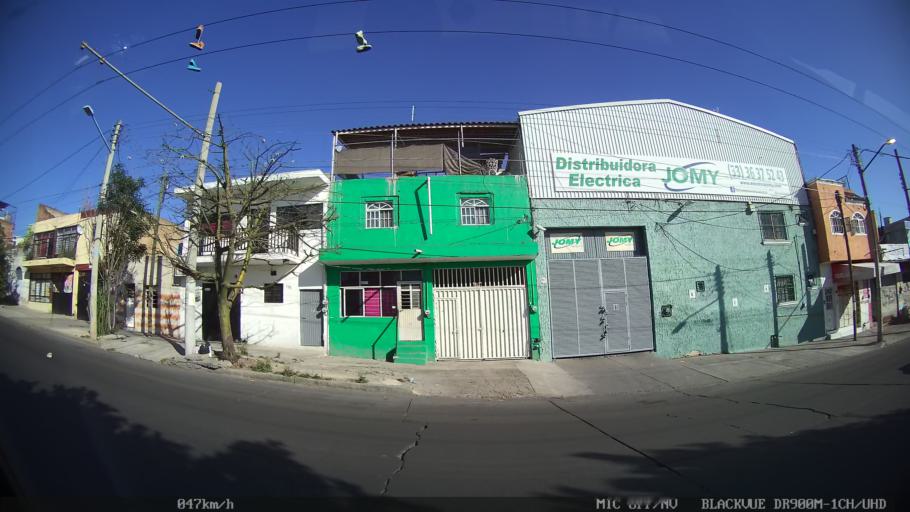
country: MX
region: Jalisco
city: Tlaquepaque
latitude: 20.6926
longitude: -103.3090
